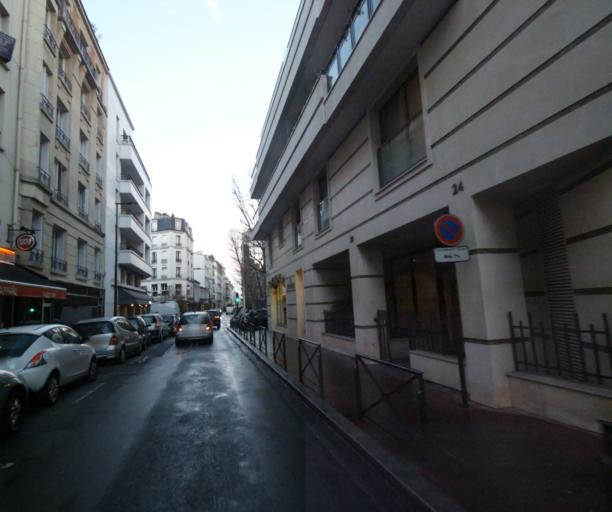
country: FR
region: Ile-de-France
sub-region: Departement des Hauts-de-Seine
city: Levallois-Perret
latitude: 48.8901
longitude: 2.2913
